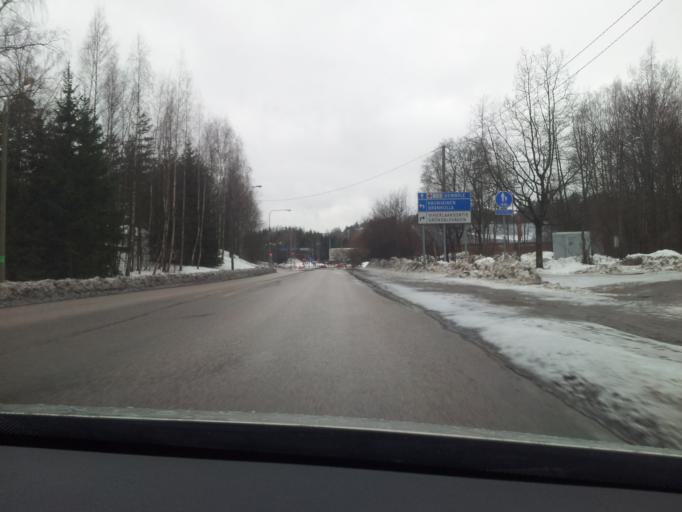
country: FI
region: Uusimaa
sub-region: Helsinki
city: Kauniainen
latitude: 60.2256
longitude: 24.7458
